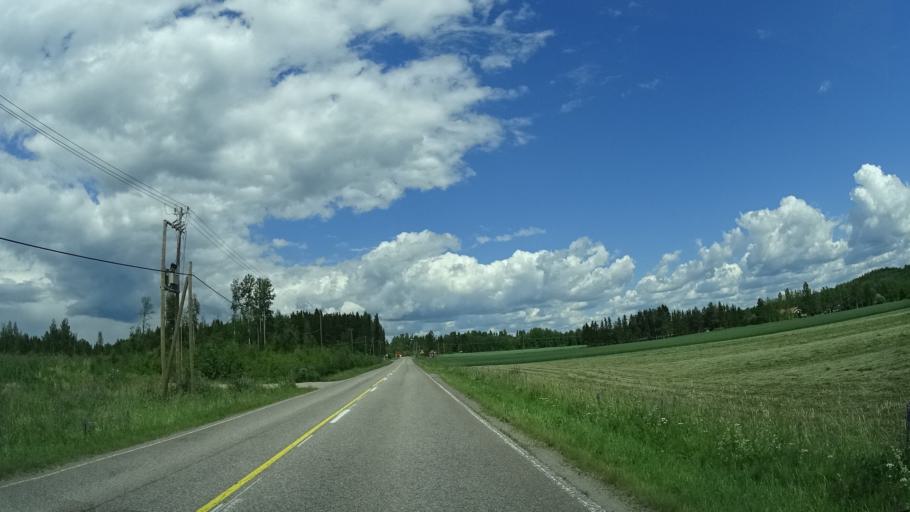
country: FI
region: Uusimaa
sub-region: Helsinki
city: Espoo
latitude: 60.3690
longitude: 24.6413
